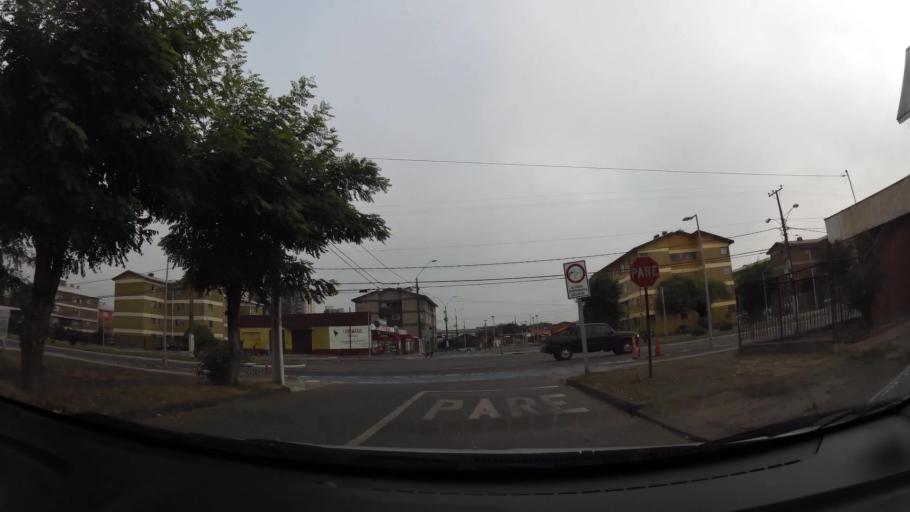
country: CL
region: Biobio
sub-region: Provincia de Concepcion
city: Concepcion
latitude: -36.7903
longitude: -73.0888
